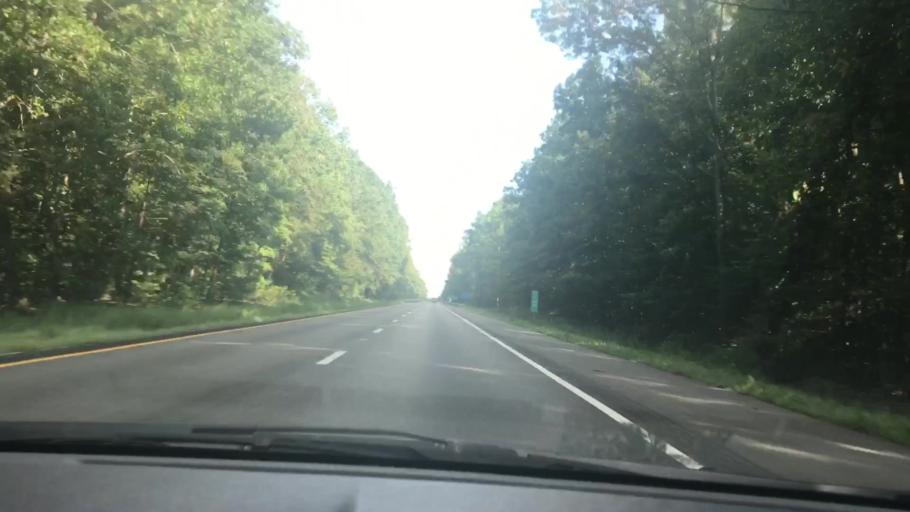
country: US
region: Virginia
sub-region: Goochland County
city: Goochland
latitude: 37.7730
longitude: -77.8790
